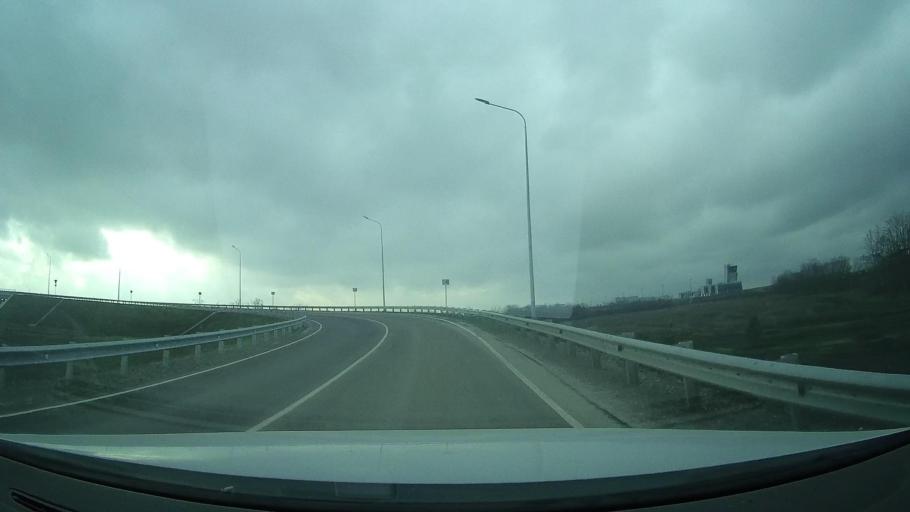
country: RU
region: Rostov
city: Grushevskaya
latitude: 47.4950
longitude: 39.9507
